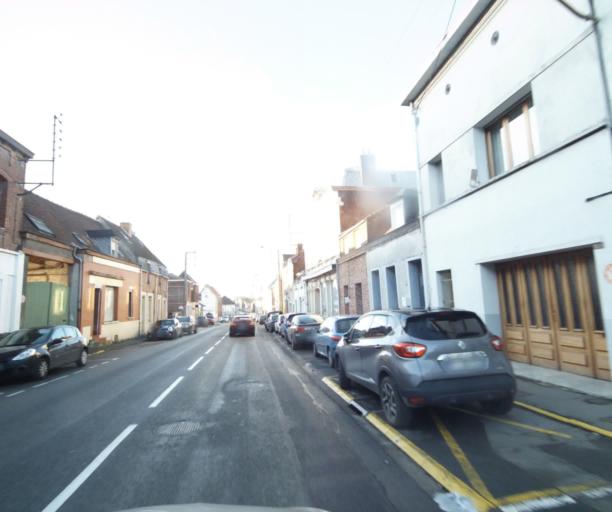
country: FR
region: Nord-Pas-de-Calais
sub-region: Departement du Nord
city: Valenciennes
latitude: 50.3517
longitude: 3.5383
